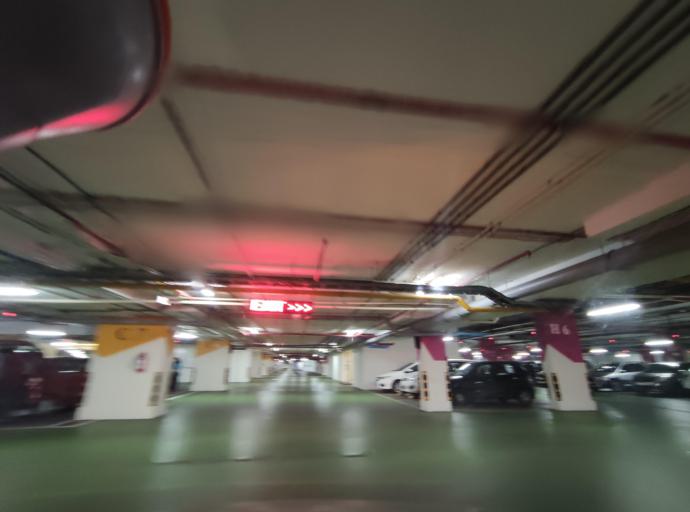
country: IN
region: Kerala
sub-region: Thiruvananthapuram
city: Thiruvananthapuram
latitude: 8.5152
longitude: 76.8976
